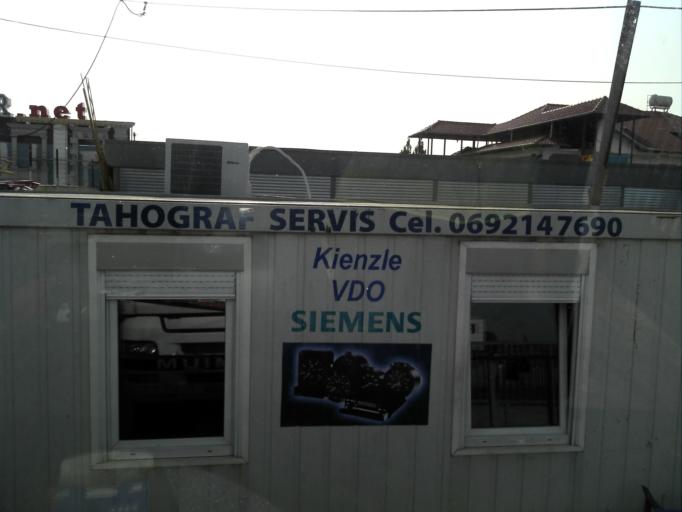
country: AL
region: Tirane
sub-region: Rrethi i Tiranes
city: Paskuqan
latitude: 41.3406
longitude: 19.7819
